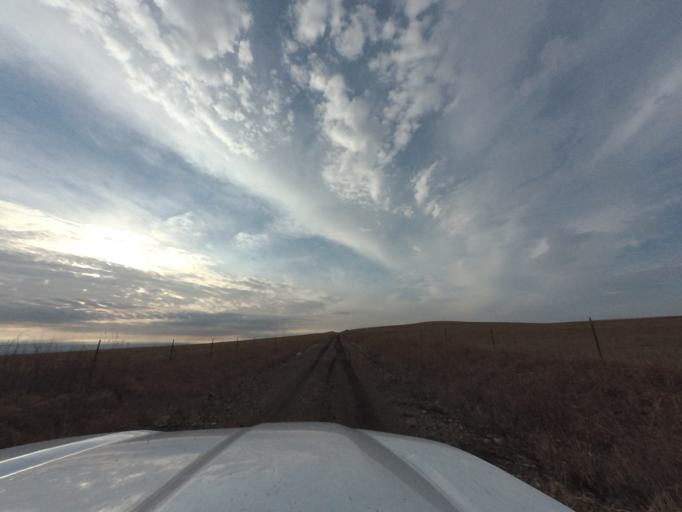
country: US
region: Kansas
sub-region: Chase County
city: Cottonwood Falls
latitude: 38.4718
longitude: -96.4471
